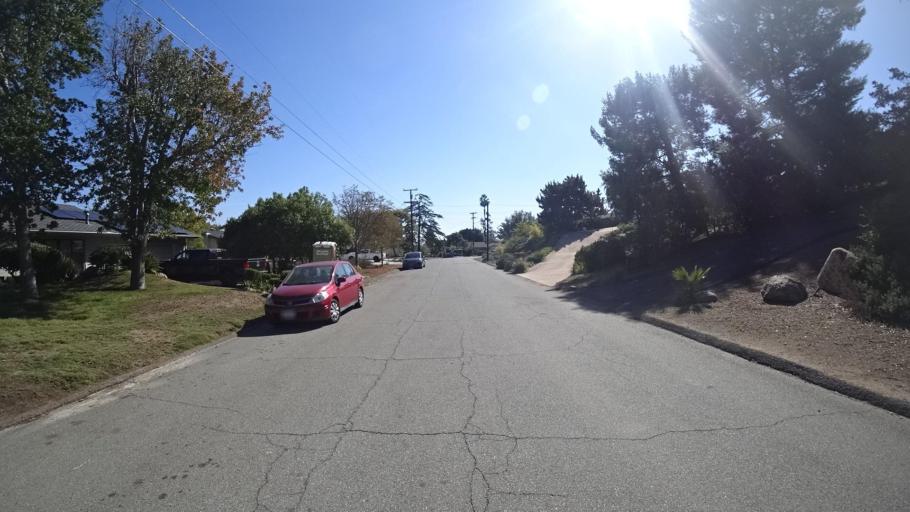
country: US
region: California
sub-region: San Diego County
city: Casa de Oro-Mount Helix
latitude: 32.7609
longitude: -116.9759
